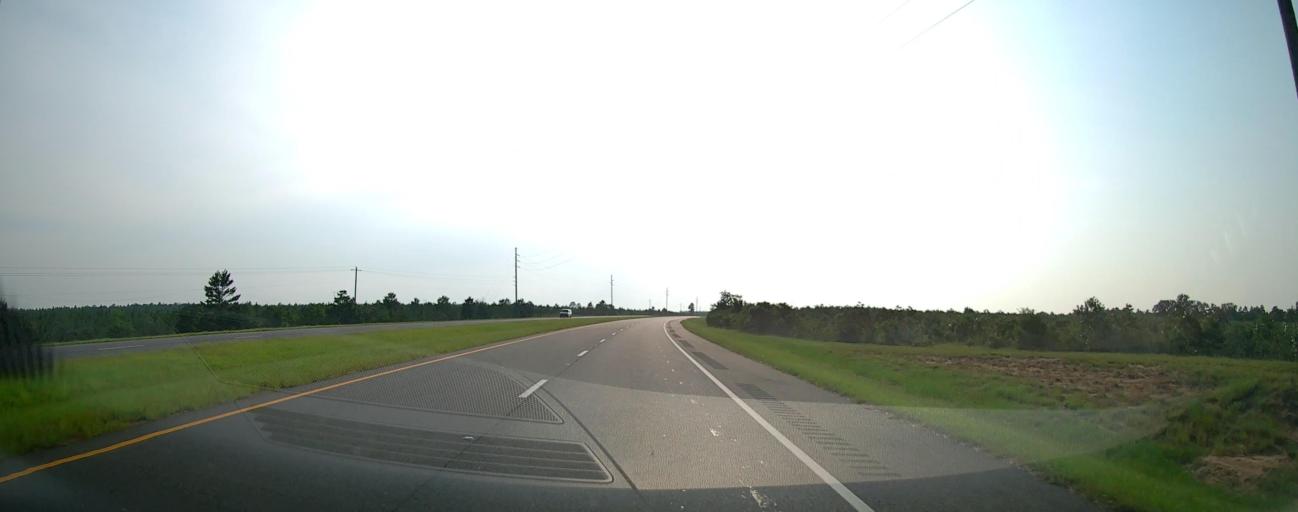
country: US
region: Georgia
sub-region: Talbot County
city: Talbotton
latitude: 32.5949
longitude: -84.4365
